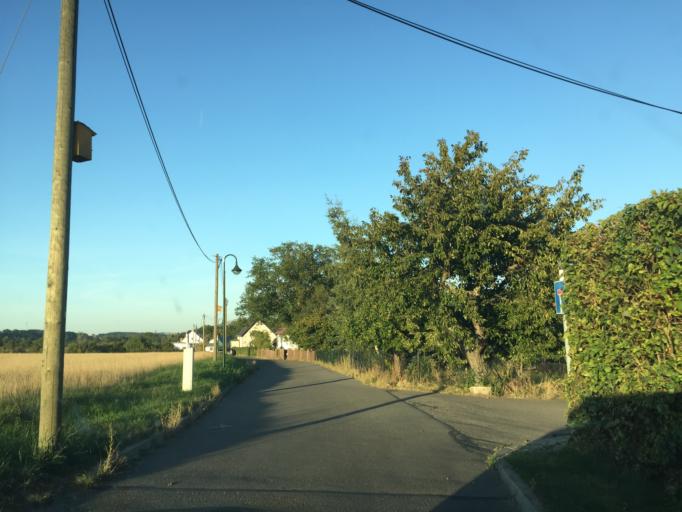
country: DE
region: Thuringia
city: Schmolln
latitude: 50.8775
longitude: 12.3280
